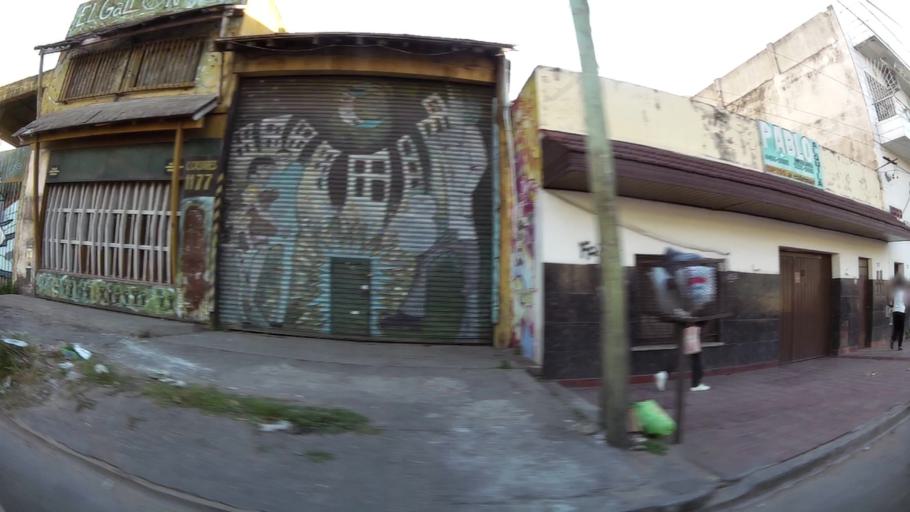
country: AR
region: Buenos Aires
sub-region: Partido de Moron
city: Moron
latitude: -34.7015
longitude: -58.6208
